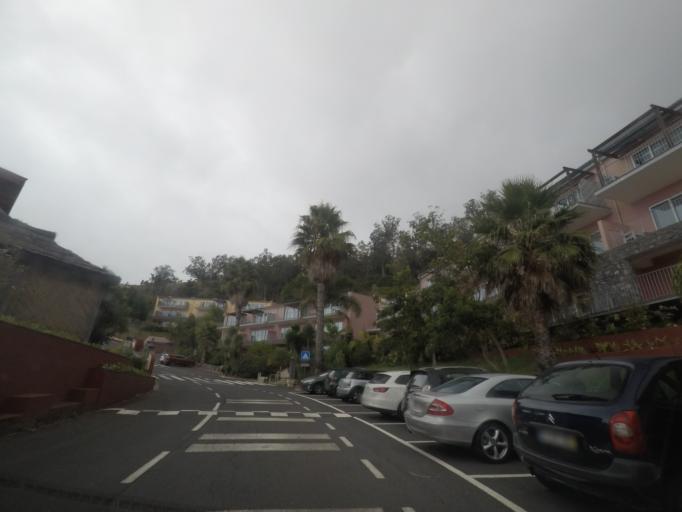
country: PT
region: Madeira
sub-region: Ribeira Brava
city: Campanario
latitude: 32.6583
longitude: -17.0032
